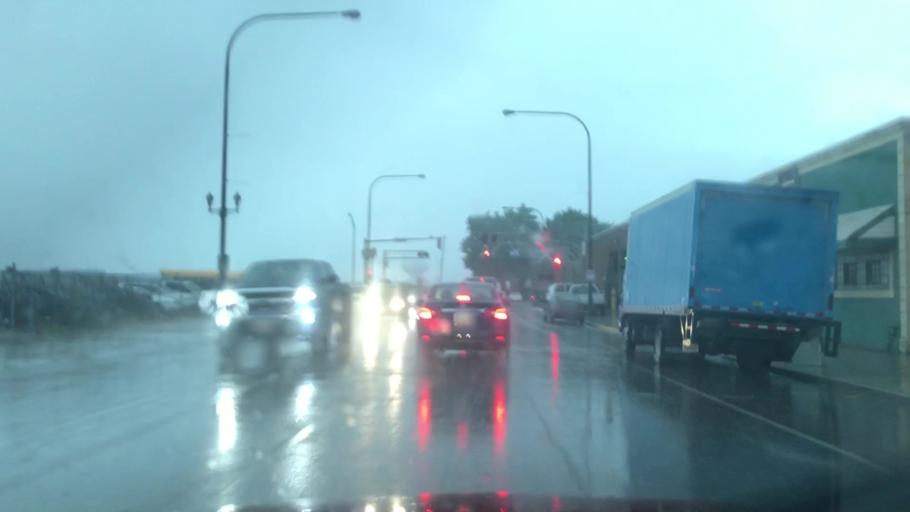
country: US
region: Illinois
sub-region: Cook County
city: Cicero
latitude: 41.8577
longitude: -87.7542
